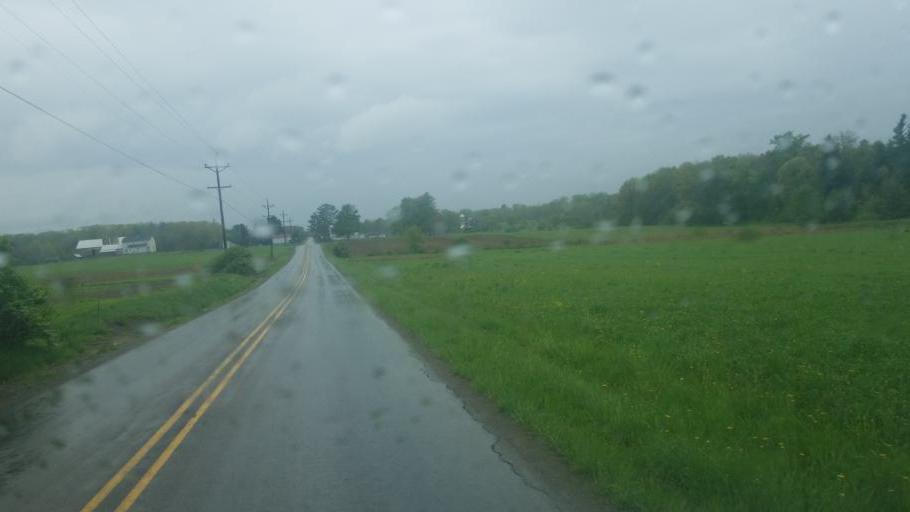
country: US
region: Pennsylvania
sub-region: Forest County
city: Tionesta
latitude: 41.3955
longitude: -79.3717
